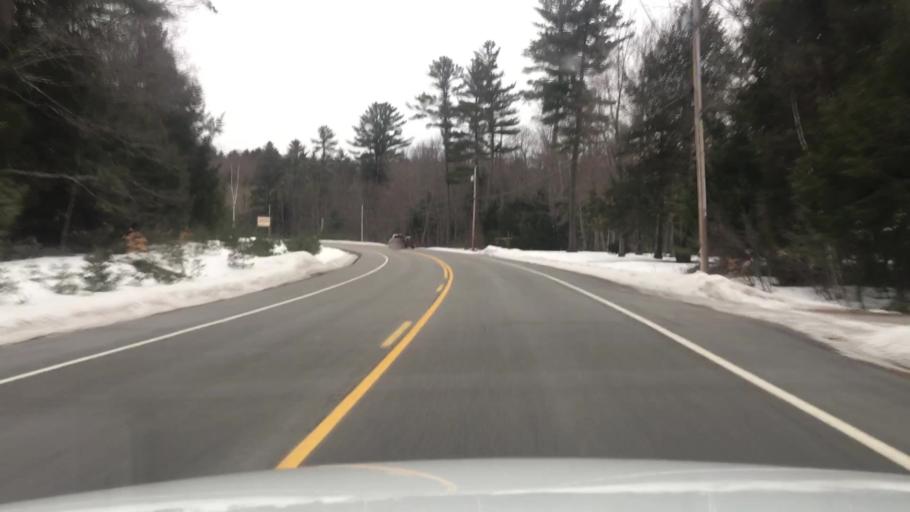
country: US
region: Maine
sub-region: York County
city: Limerick
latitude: 43.7249
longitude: -70.8132
